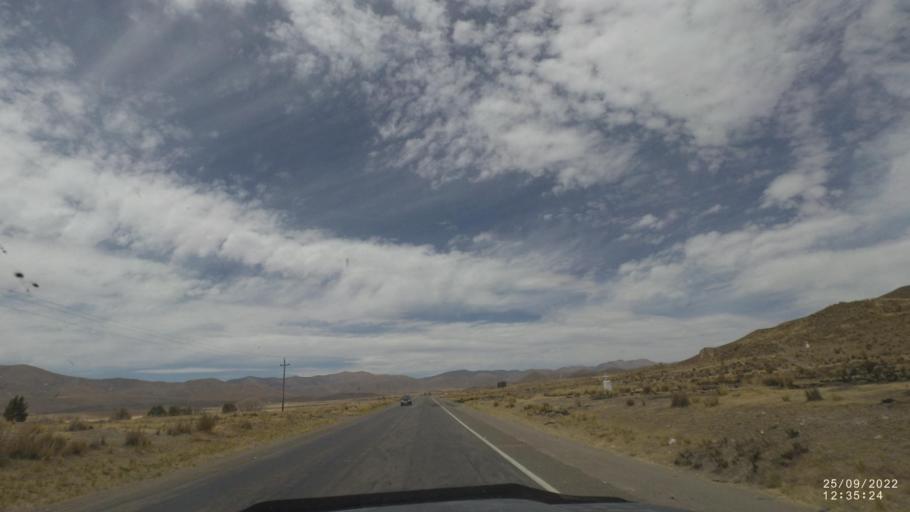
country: BO
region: Oruro
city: Machacamarca
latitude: -18.1638
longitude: -67.0044
